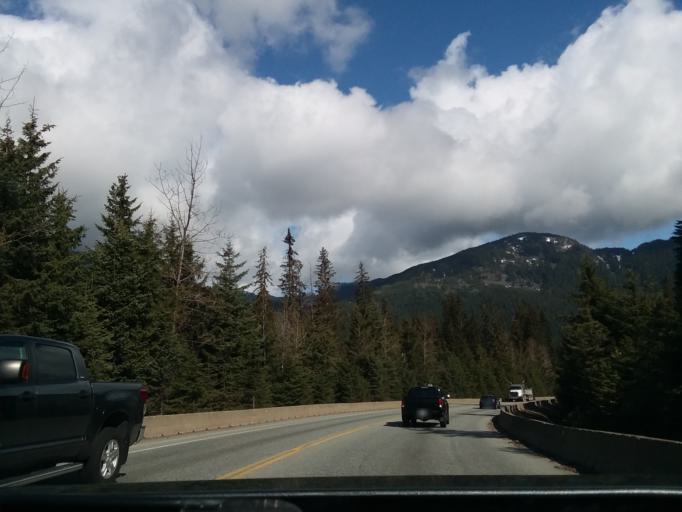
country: CA
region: British Columbia
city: Whistler
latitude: 50.1391
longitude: -122.9563
